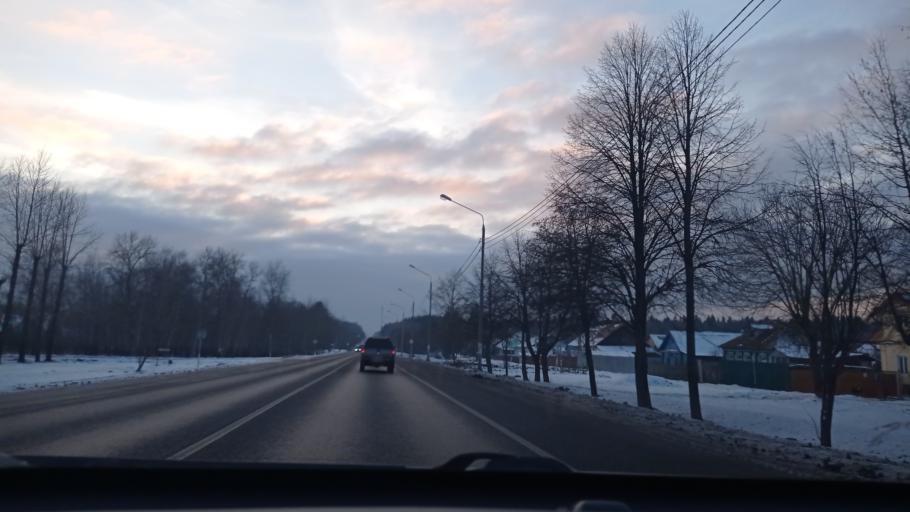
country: RU
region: Moskovskaya
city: Selyatino
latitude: 55.2607
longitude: 37.0999
